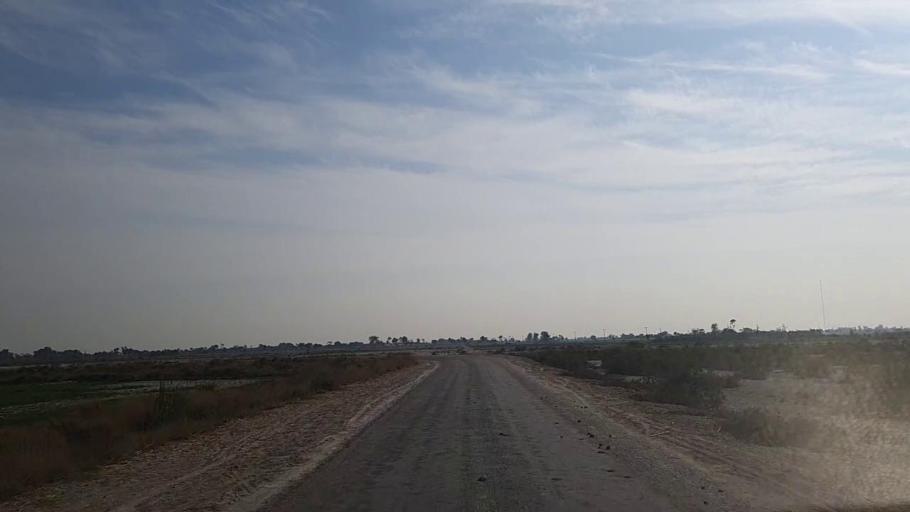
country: PK
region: Sindh
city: Daur
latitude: 26.4791
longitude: 68.4127
